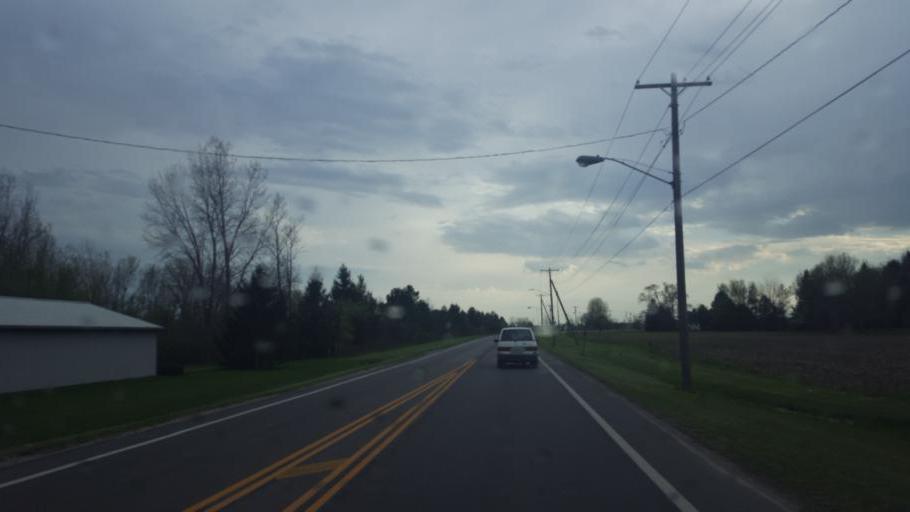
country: US
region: Ohio
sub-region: Wyandot County
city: Carey
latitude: 40.9458
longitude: -83.3889
